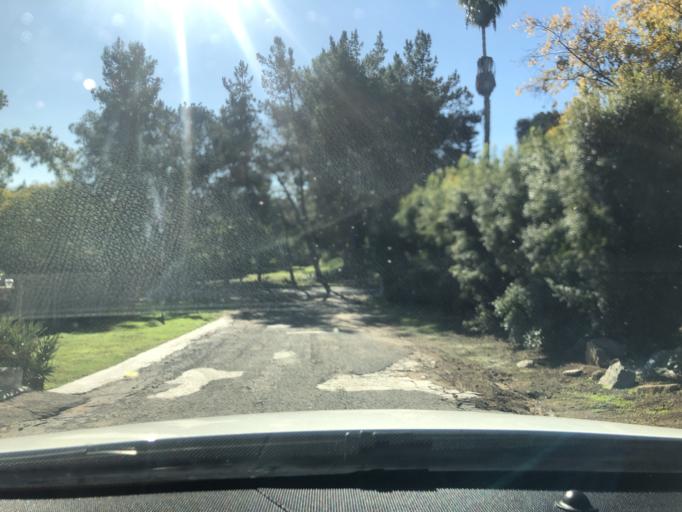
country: US
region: California
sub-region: San Diego County
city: Casa de Oro-Mount Helix
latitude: 32.7735
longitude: -116.9463
